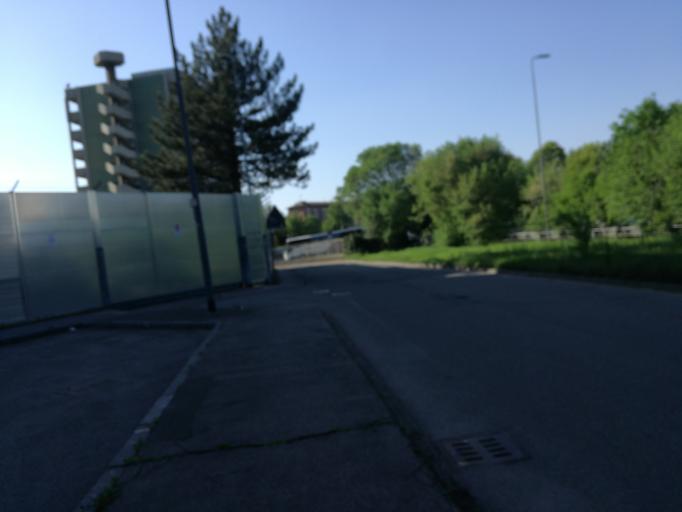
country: IT
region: Lombardy
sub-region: Citta metropolitana di Milano
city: Milano
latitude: 45.4357
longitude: 9.1906
